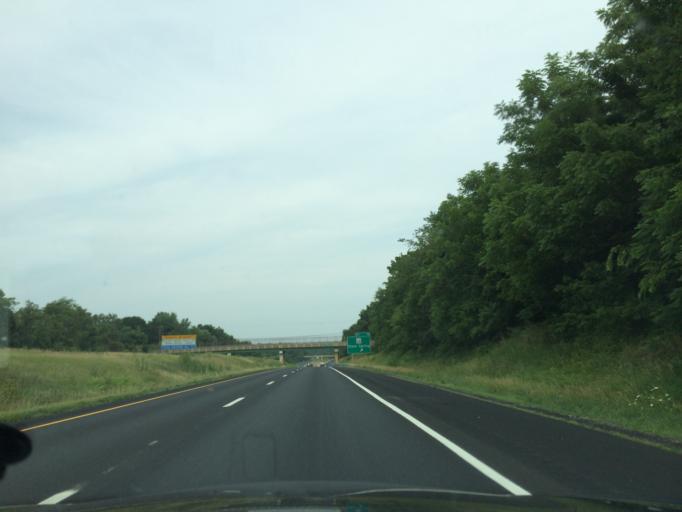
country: US
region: Maryland
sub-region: Washington County
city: Wilson-Conococheague
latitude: 39.6482
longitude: -77.9328
